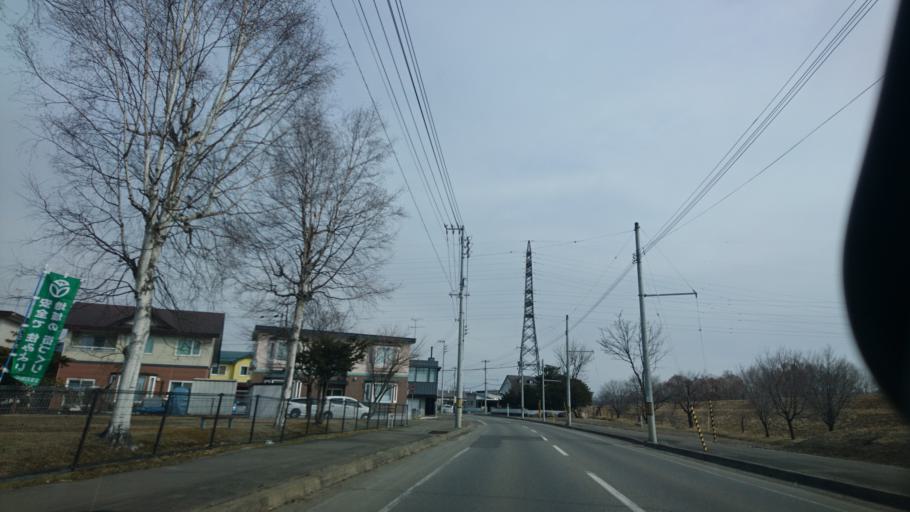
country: JP
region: Hokkaido
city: Otofuke
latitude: 42.9630
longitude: 143.2130
